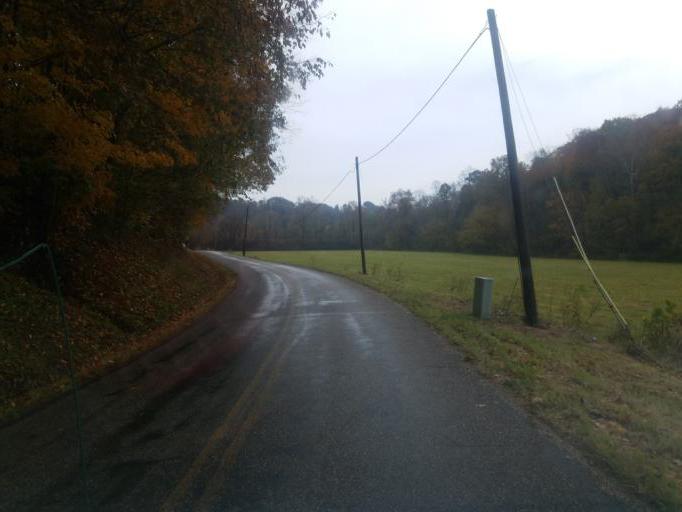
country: US
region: Ohio
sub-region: Washington County
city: Beverly
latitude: 39.5494
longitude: -81.6531
